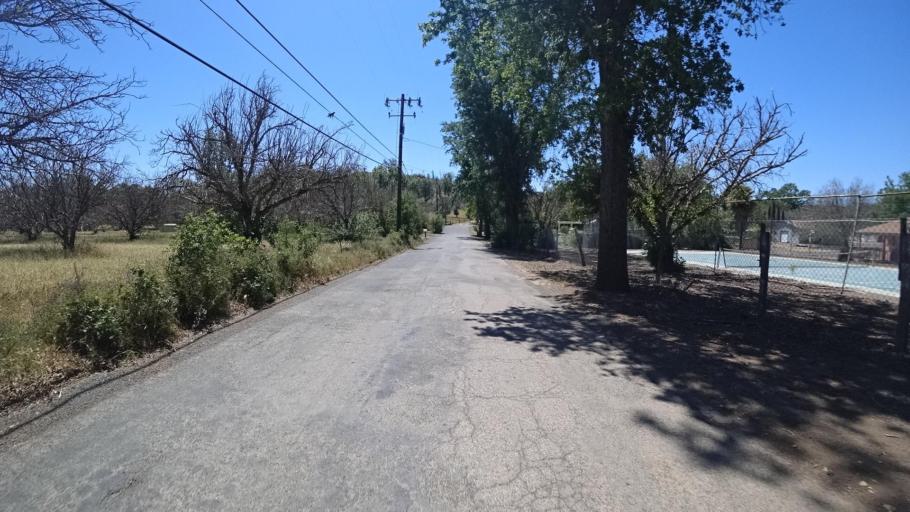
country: US
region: California
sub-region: Lake County
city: Lower Lake
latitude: 38.9100
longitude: -122.5901
